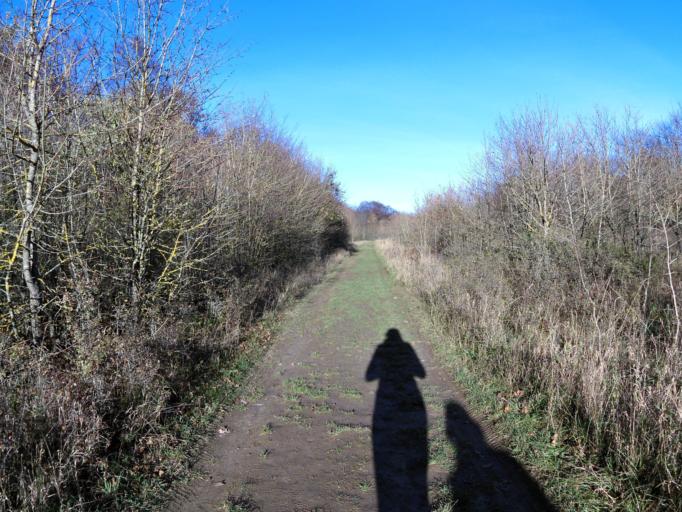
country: DE
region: Thuringia
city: Kammerforst
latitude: 51.0570
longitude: 10.4436
